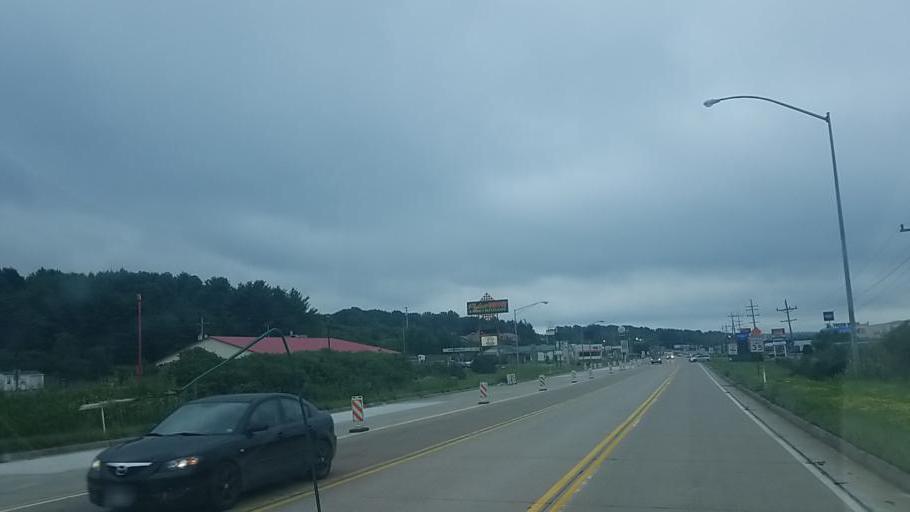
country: US
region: Pennsylvania
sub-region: Jefferson County
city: Brookville
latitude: 41.1689
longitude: -79.0980
